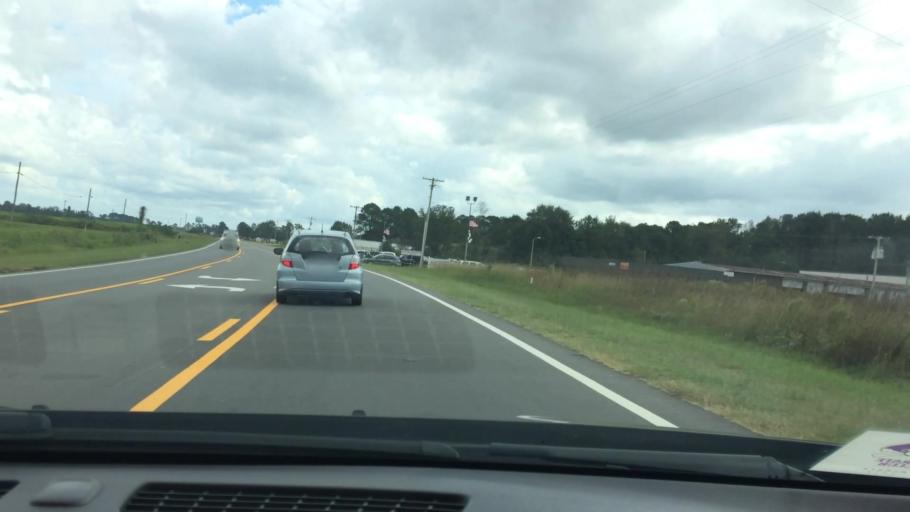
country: US
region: North Carolina
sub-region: Pitt County
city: Farmville
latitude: 35.6066
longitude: -77.6547
